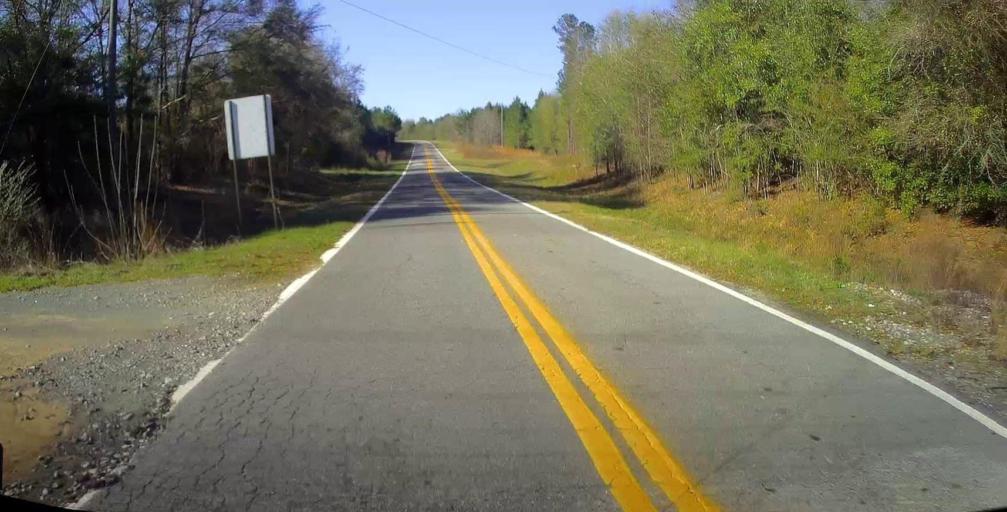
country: US
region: Georgia
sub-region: Taylor County
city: Reynolds
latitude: 32.5504
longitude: -83.9979
